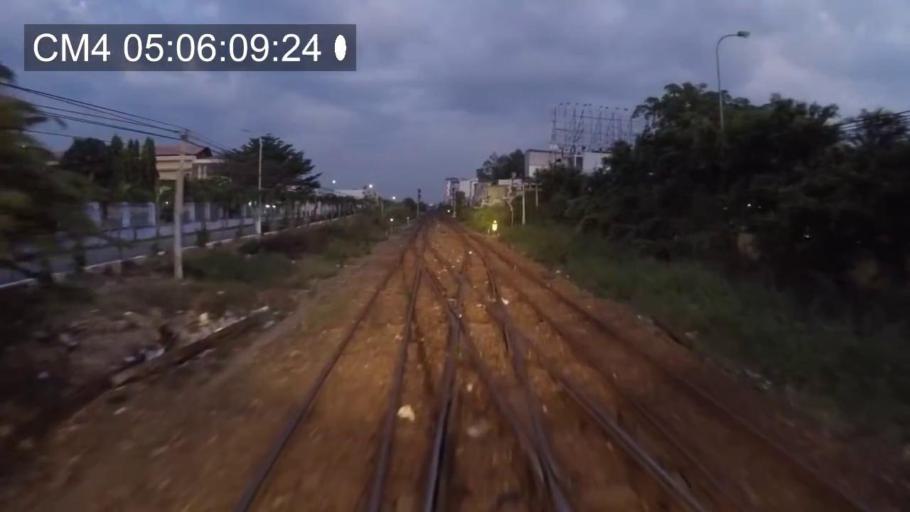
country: VN
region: Khanh Hoa
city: Nha Trang
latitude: 12.2758
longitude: 109.1787
